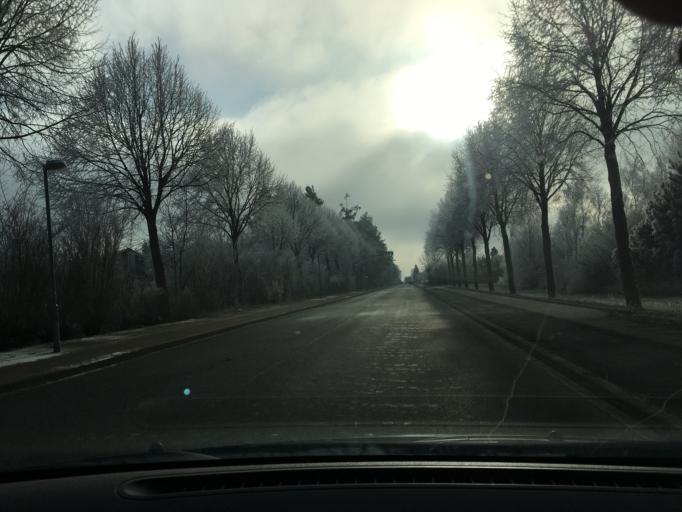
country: DE
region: Lower Saxony
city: Lueneburg
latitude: 53.2622
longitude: 10.3909
